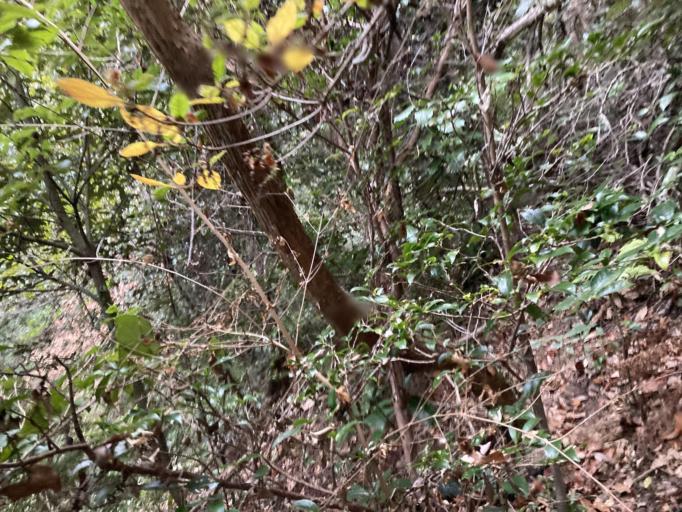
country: JP
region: Nara
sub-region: Ikoma-shi
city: Ikoma
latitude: 34.6926
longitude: 135.6851
